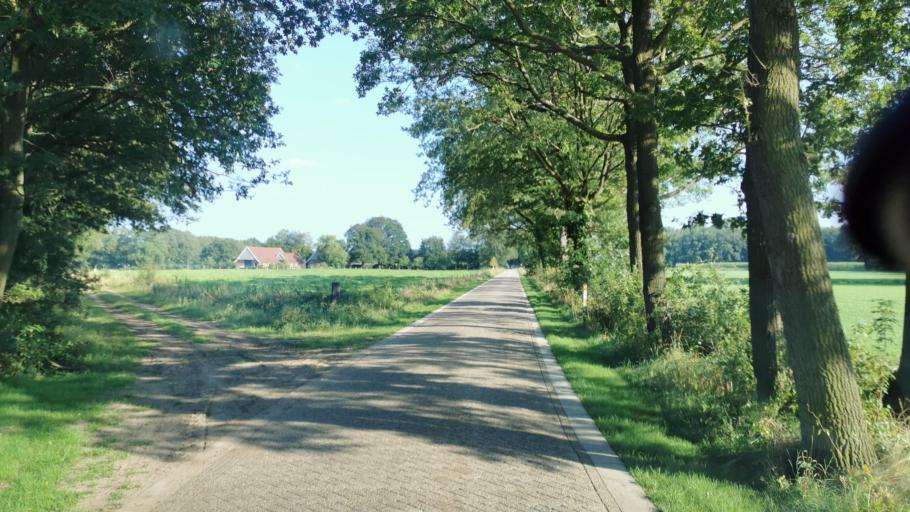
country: NL
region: Overijssel
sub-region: Gemeente Tubbergen
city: Tubbergen
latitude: 52.3464
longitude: 6.8398
